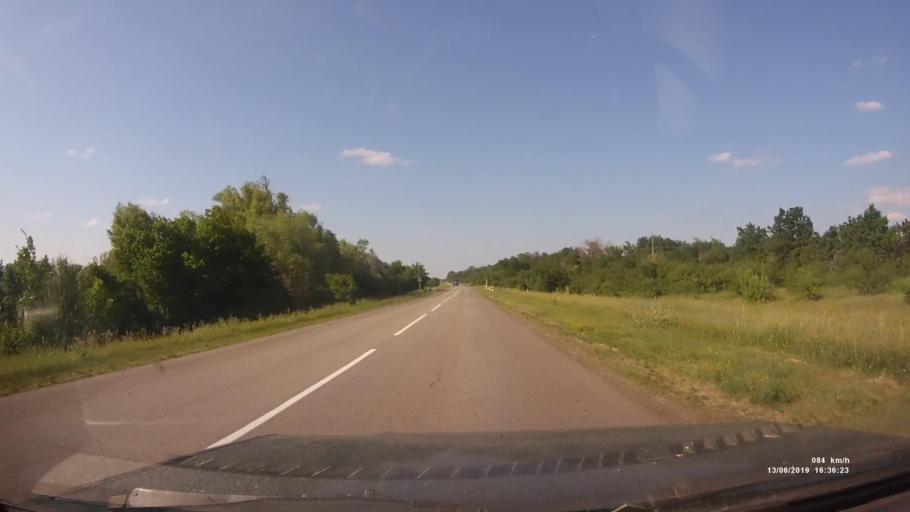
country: RU
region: Rostov
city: Kazanskaya
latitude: 49.8942
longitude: 41.3055
